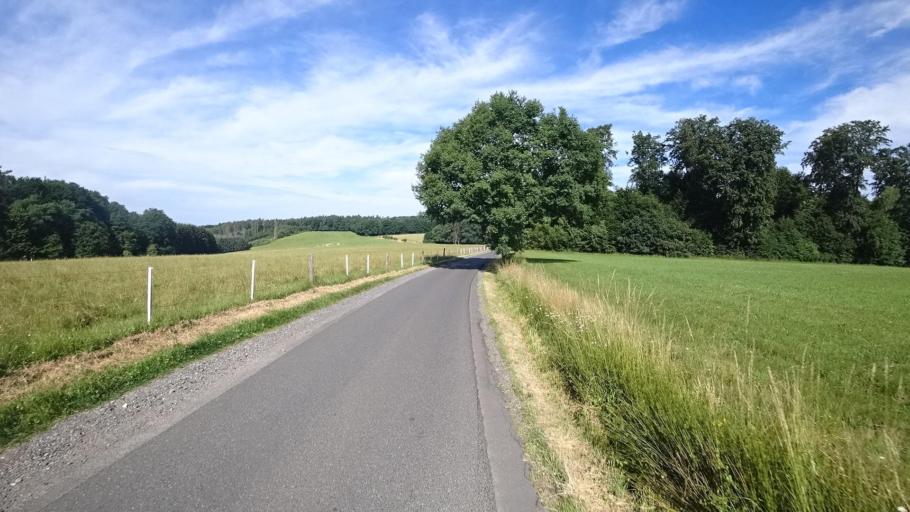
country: DE
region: Rheinland-Pfalz
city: Ratzert
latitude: 50.6564
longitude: 7.6064
